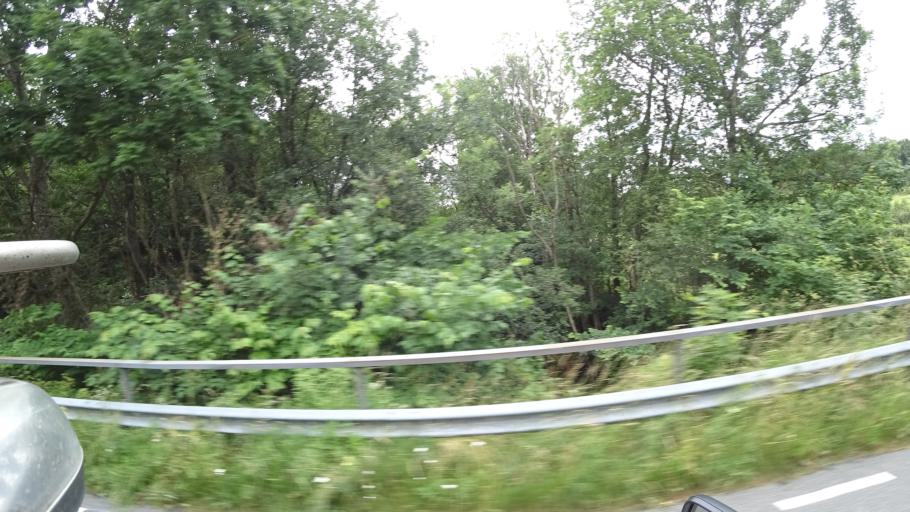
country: SE
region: Skane
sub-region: Kristianstads Kommun
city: Degeberga
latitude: 55.7146
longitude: 13.9853
